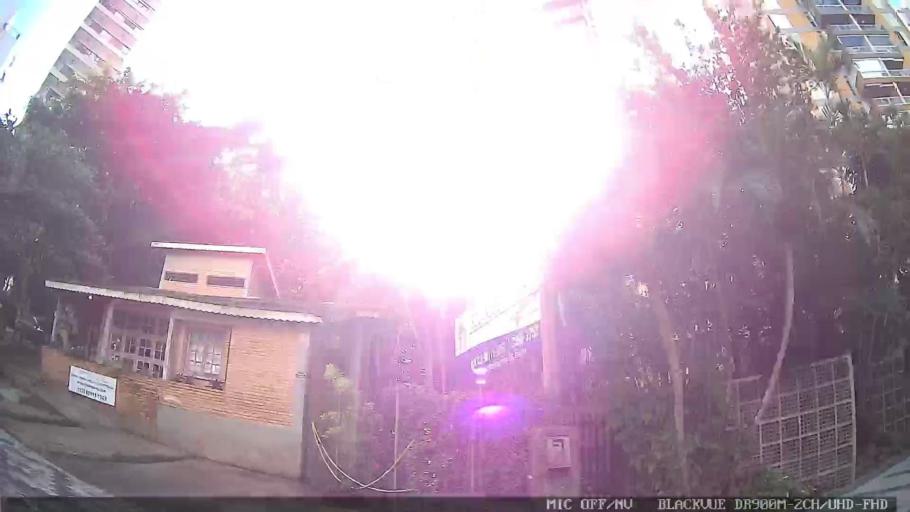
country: BR
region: Sao Paulo
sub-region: Guaruja
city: Guaruja
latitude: -23.9937
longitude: -46.2525
